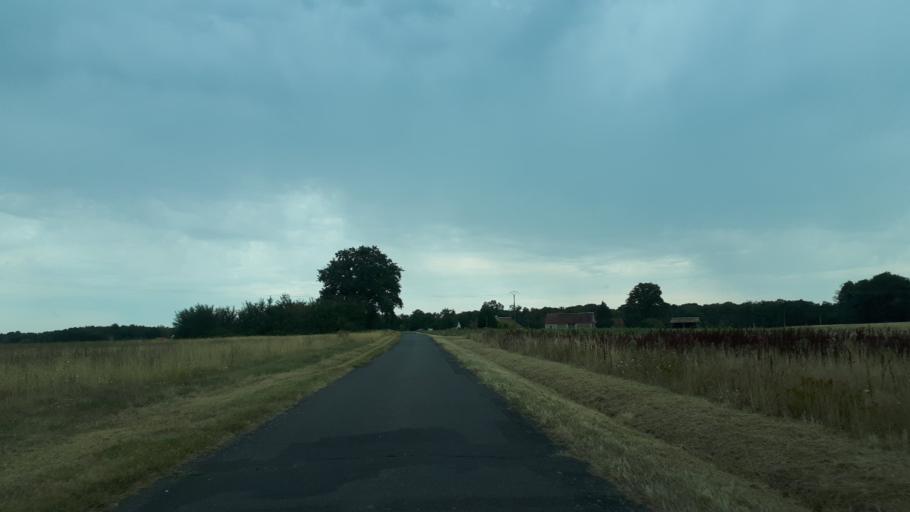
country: FR
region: Centre
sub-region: Departement du Loir-et-Cher
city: Saint-Romain-sur-Cher
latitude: 47.3574
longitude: 1.4016
